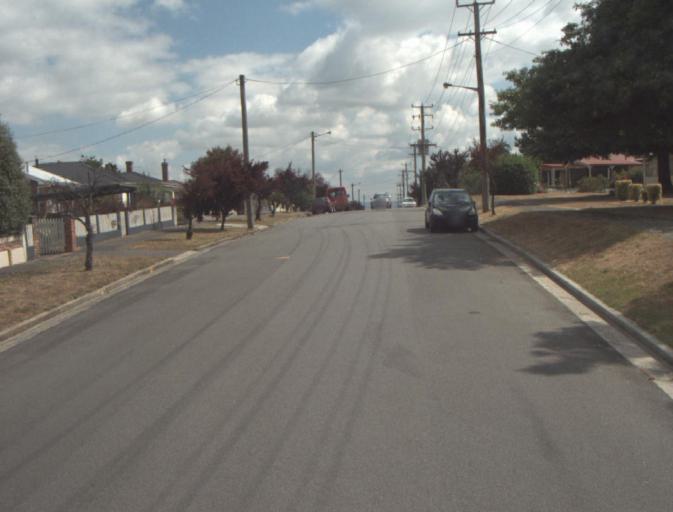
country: AU
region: Tasmania
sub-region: Launceston
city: Summerhill
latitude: -41.4636
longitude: 147.1484
